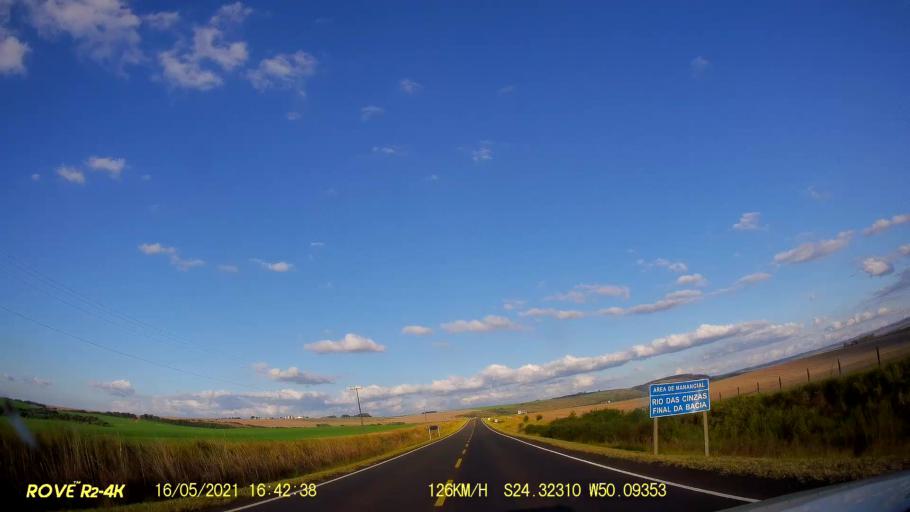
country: BR
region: Parana
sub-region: Pirai Do Sul
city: Pirai do Sul
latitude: -24.3237
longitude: -50.0936
